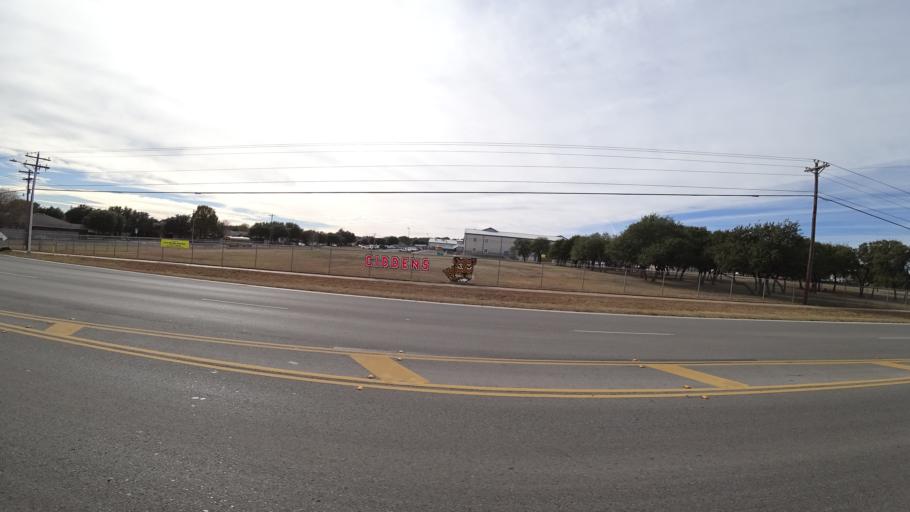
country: US
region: Texas
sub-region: Williamson County
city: Cedar Park
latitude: 30.5244
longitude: -97.8427
